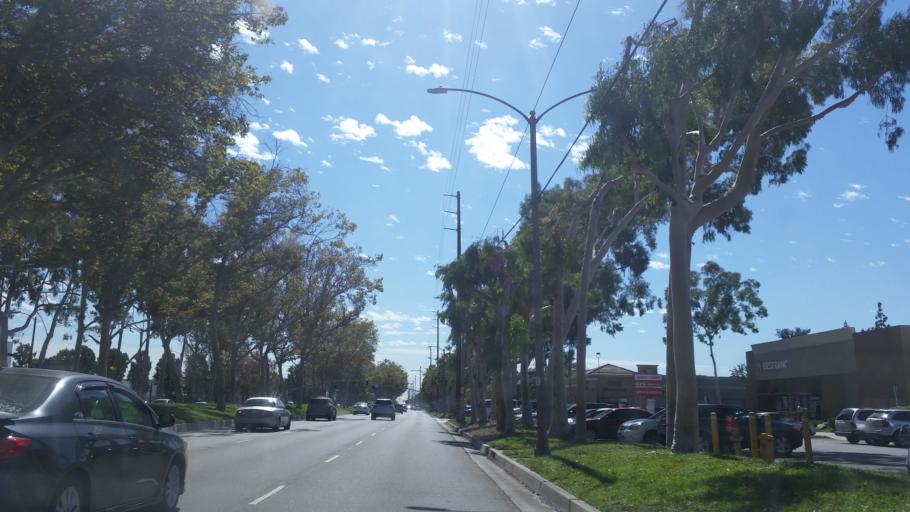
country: US
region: California
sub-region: Los Angeles County
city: Lakewood
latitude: 33.8525
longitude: -118.1427
